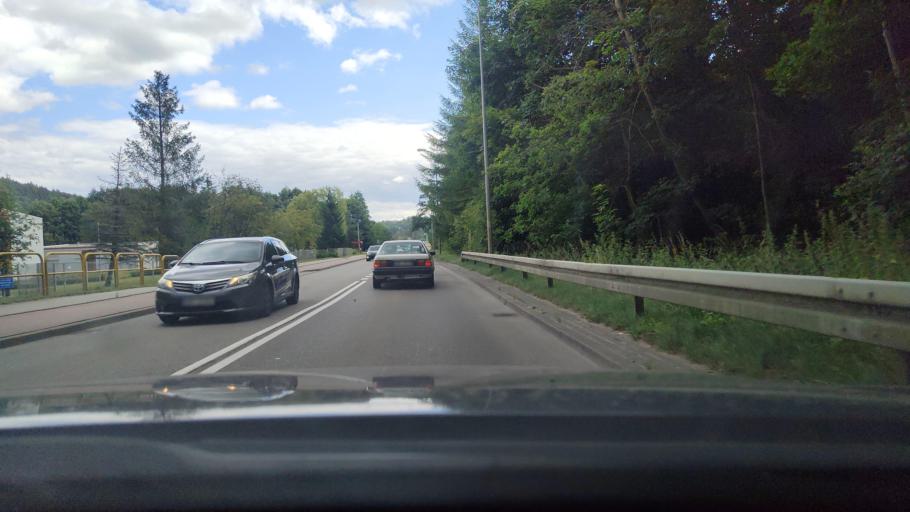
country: PL
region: Pomeranian Voivodeship
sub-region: Powiat wejherowski
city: Wejherowo
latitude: 54.5920
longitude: 18.2387
